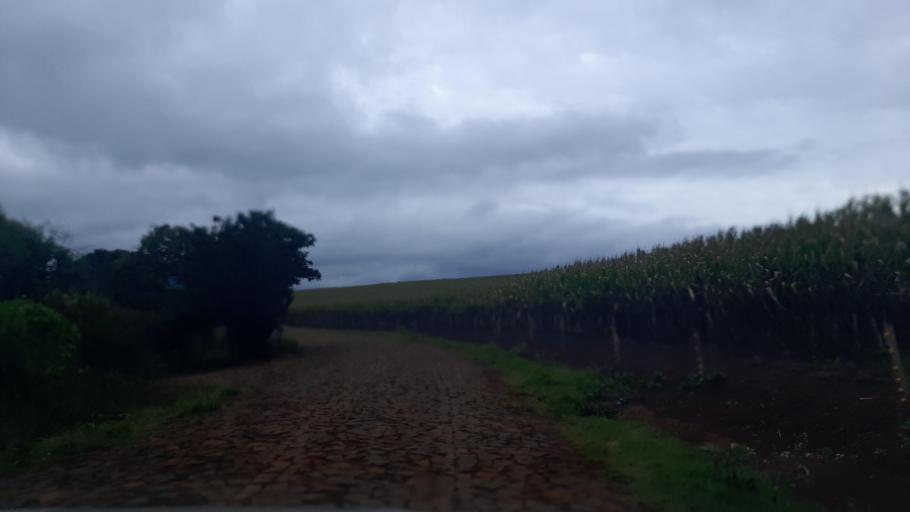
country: BR
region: Parana
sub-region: Ampere
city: Ampere
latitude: -26.0362
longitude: -53.5139
